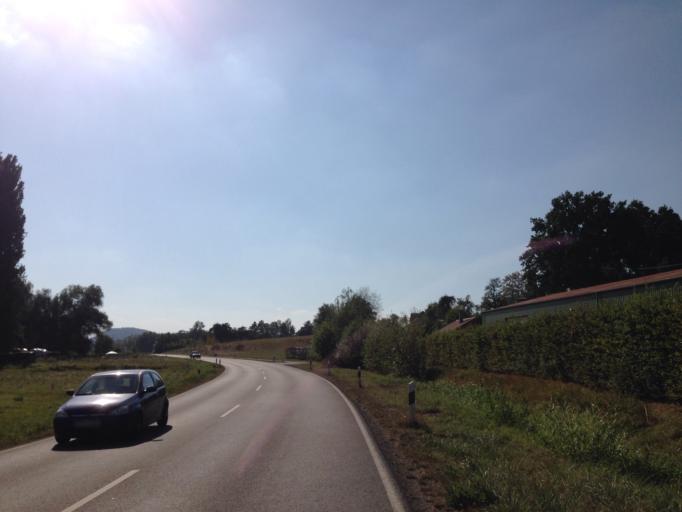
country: DE
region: Hesse
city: Staufenberg
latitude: 50.6646
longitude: 8.7540
